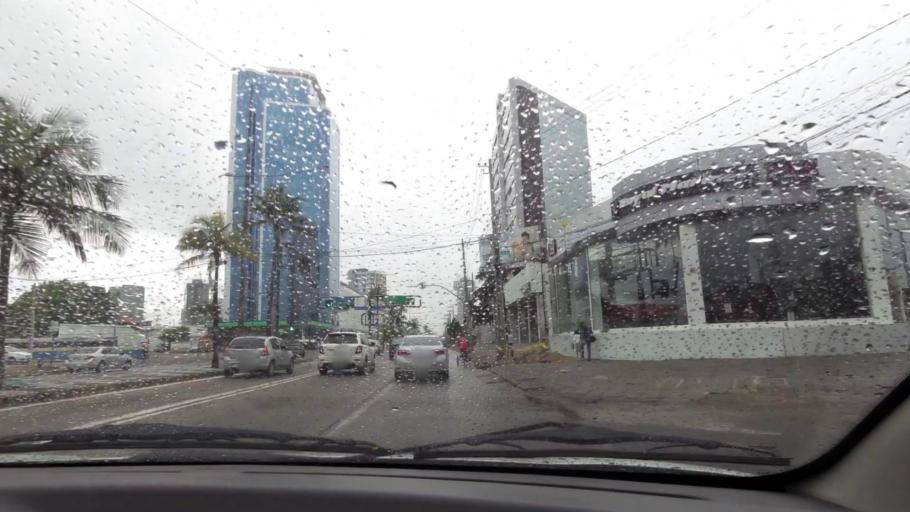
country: BR
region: Pernambuco
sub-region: Recife
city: Recife
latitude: -8.0898
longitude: -34.8823
